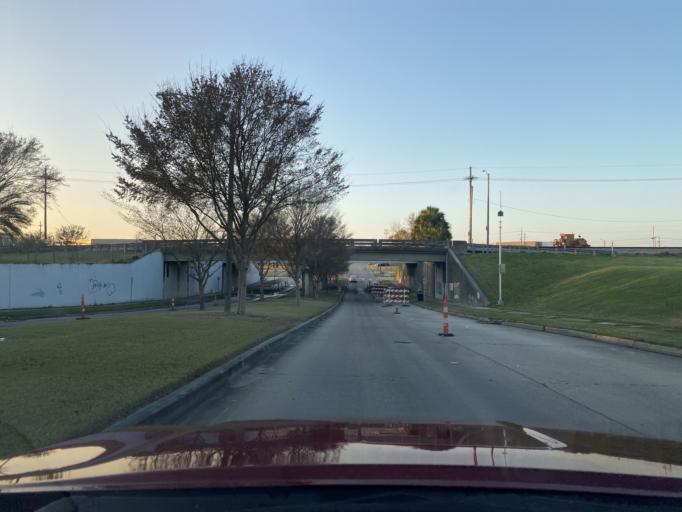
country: US
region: Louisiana
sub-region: Orleans Parish
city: New Orleans
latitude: 30.0276
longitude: -90.0442
